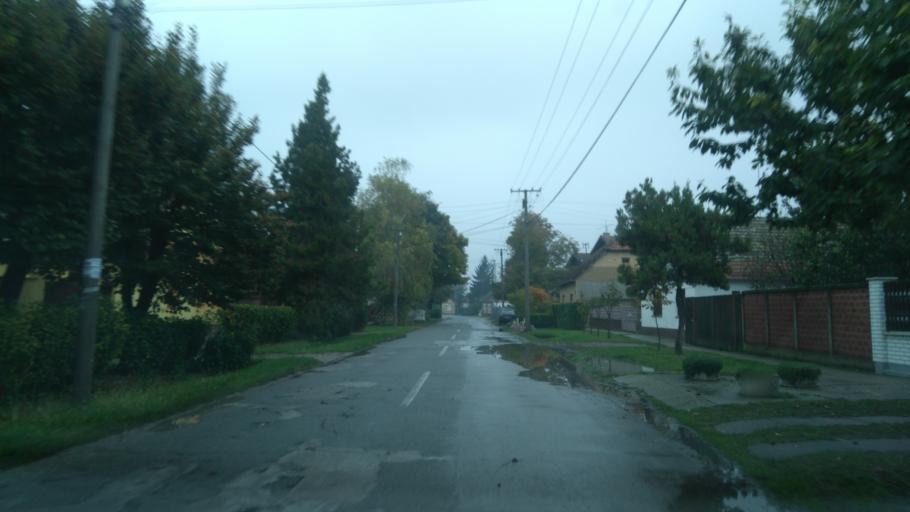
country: RS
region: Autonomna Pokrajina Vojvodina
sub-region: Juznobacki Okrug
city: Becej
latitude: 45.6183
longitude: 20.0587
